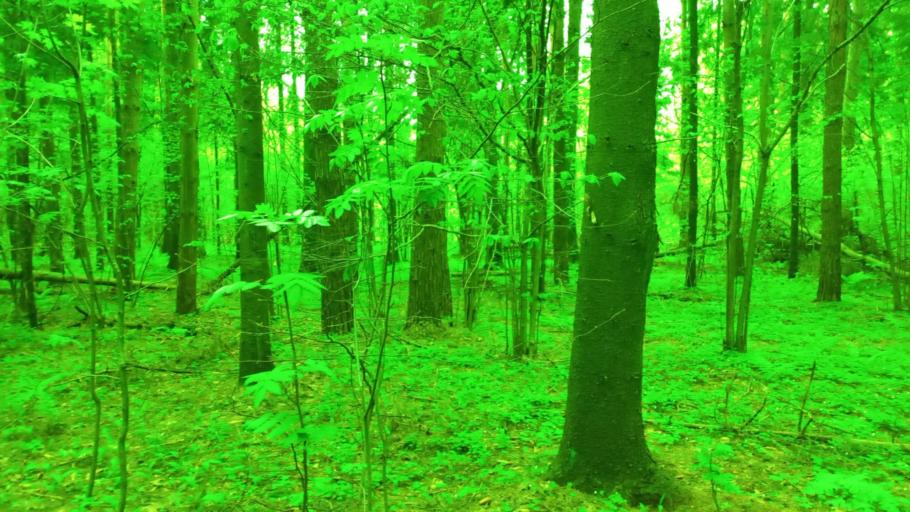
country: RU
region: Moskovskaya
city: Petrovskaya
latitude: 55.5805
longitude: 37.8031
